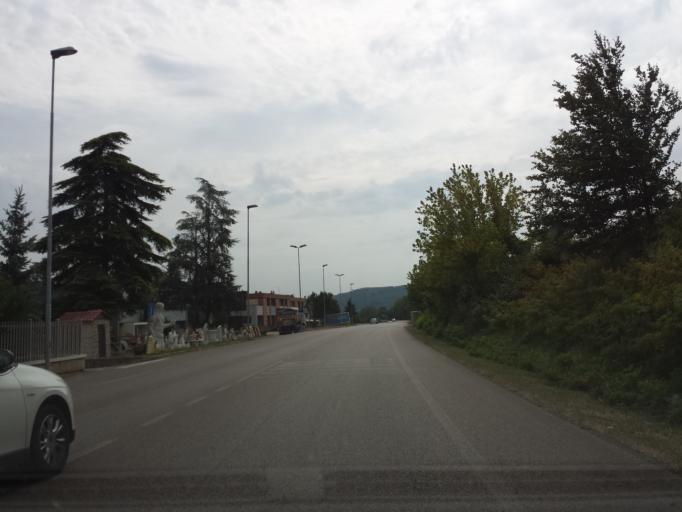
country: IT
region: Veneto
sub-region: Provincia di Verona
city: Montecchia di Crosara
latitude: 45.4739
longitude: 11.2672
